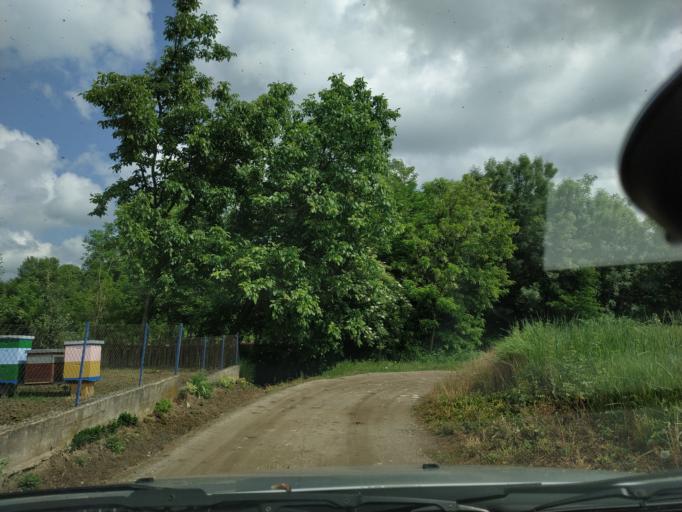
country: RS
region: Central Serbia
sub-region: Nisavski Okrug
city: Aleksinac
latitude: 43.4268
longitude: 21.5855
